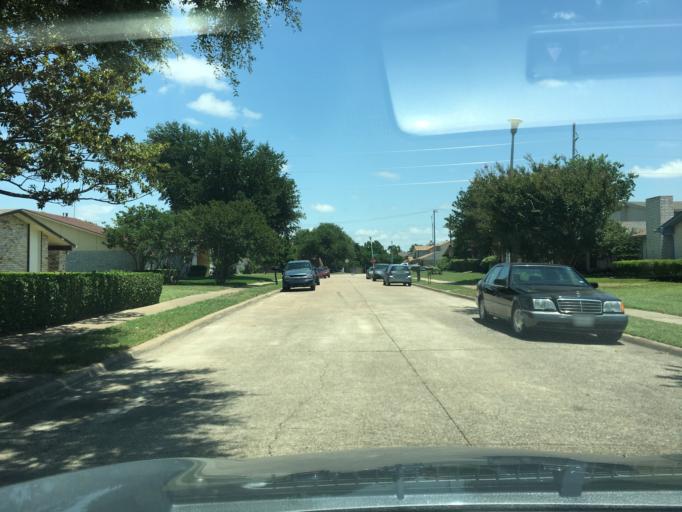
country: US
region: Texas
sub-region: Dallas County
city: Garland
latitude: 32.9497
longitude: -96.6748
